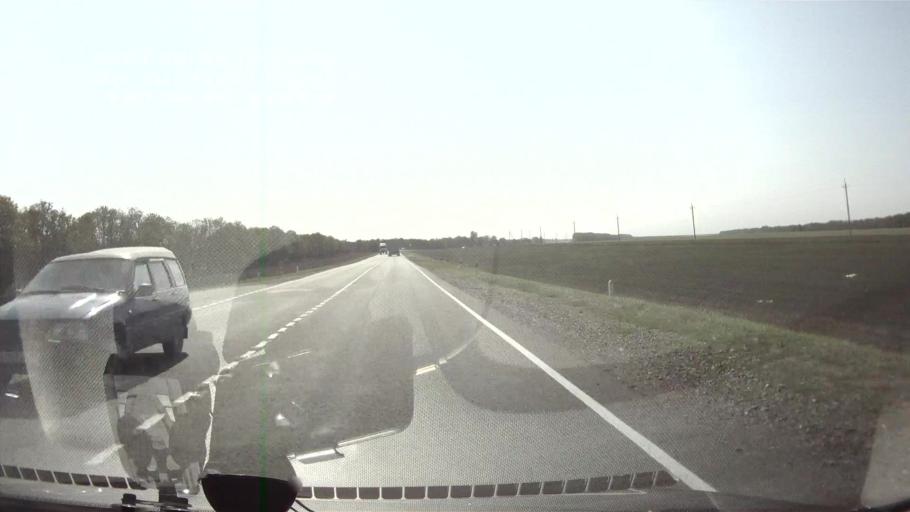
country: RU
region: Krasnodarskiy
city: Novopokrovskaya
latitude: 45.9119
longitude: 40.7190
